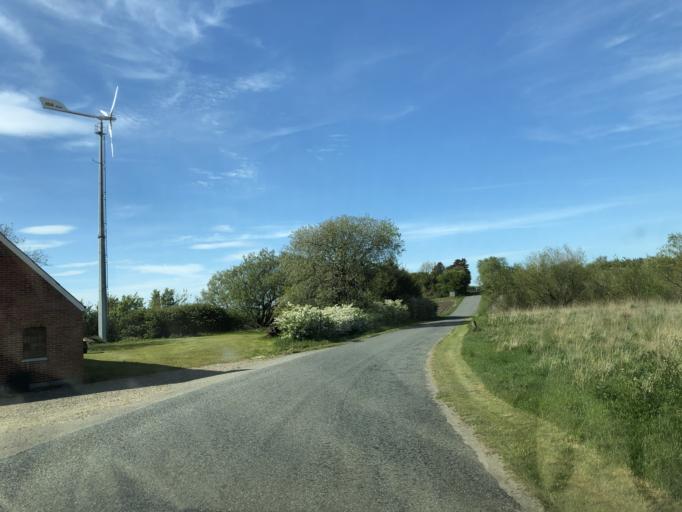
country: DK
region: Central Jutland
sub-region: Ringkobing-Skjern Kommune
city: Videbaek
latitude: 56.0954
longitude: 8.4906
